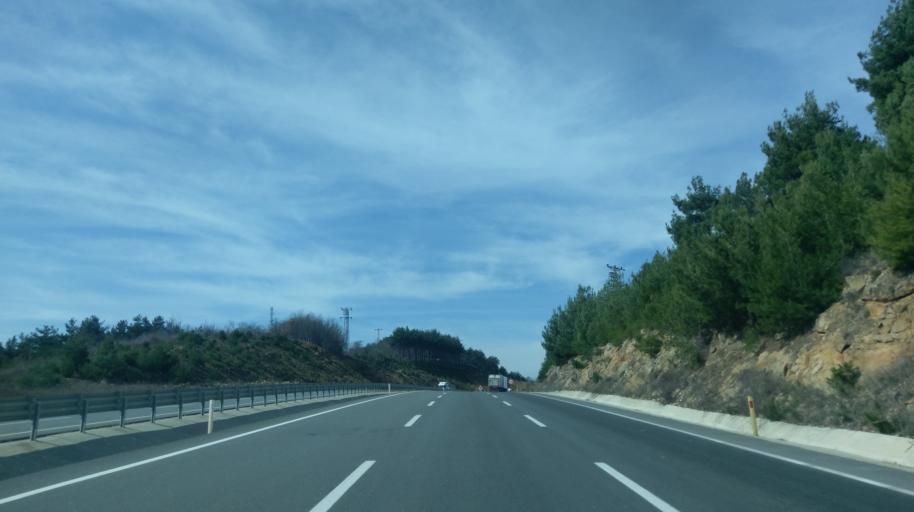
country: TR
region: Canakkale
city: Evrese
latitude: 40.7082
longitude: 26.7727
